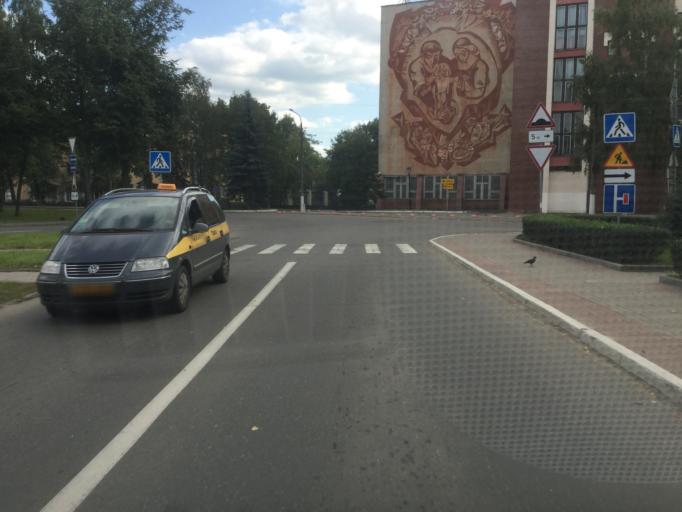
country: BY
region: Vitebsk
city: Vitebsk
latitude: 55.1971
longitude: 30.1913
